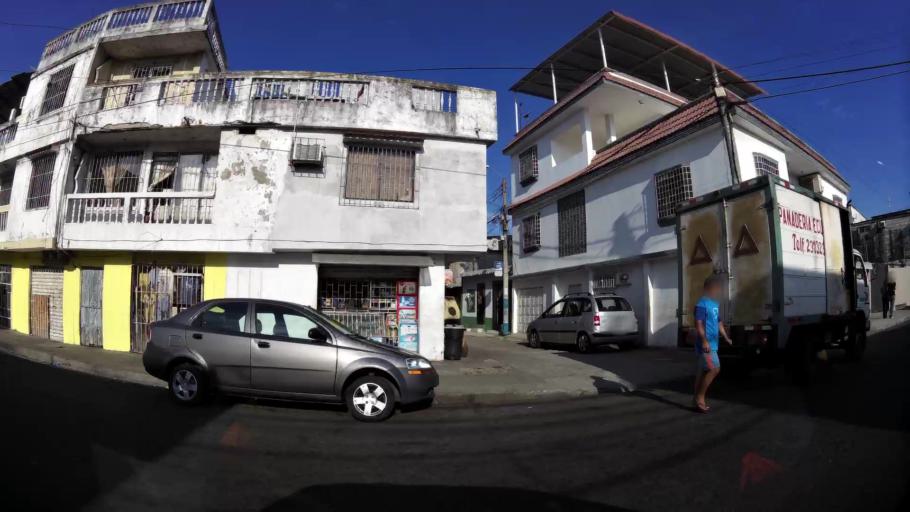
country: EC
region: Guayas
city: Guayaquil
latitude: -2.2200
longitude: -79.9041
